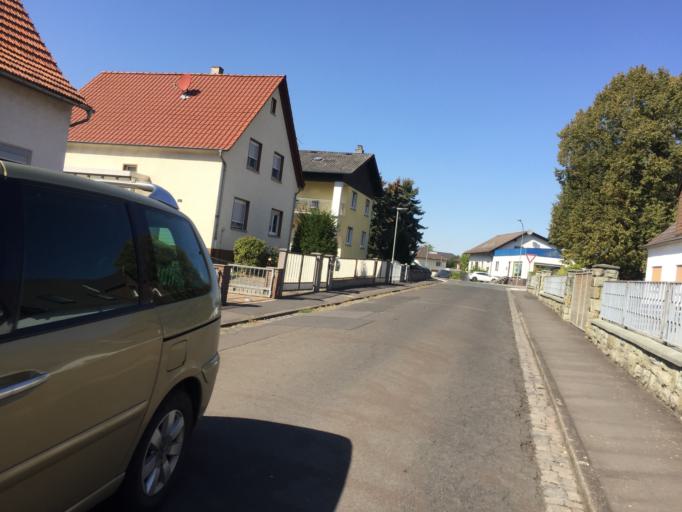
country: DE
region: Hesse
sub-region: Regierungsbezirk Giessen
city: Hungen
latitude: 50.4350
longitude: 8.8820
